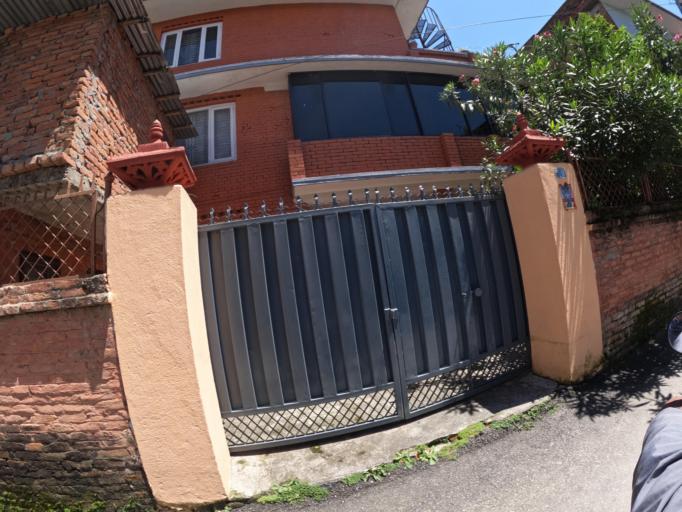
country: NP
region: Central Region
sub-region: Bagmati Zone
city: Kathmandu
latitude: 27.7434
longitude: 85.3256
